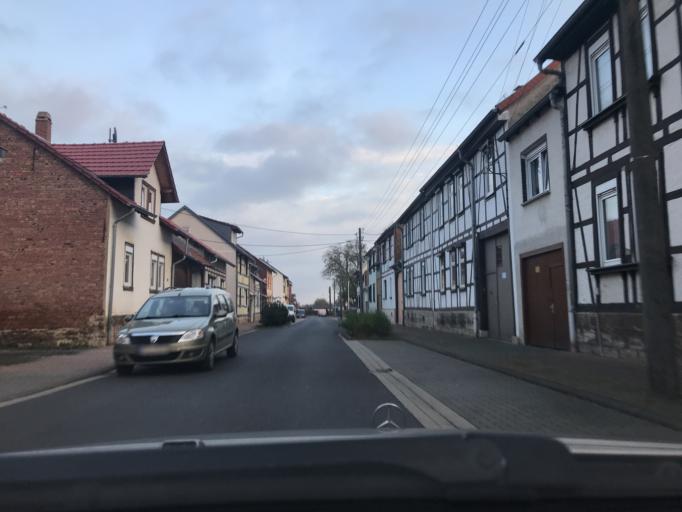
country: DE
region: Thuringia
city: Muehlhausen
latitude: 51.2108
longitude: 10.4903
